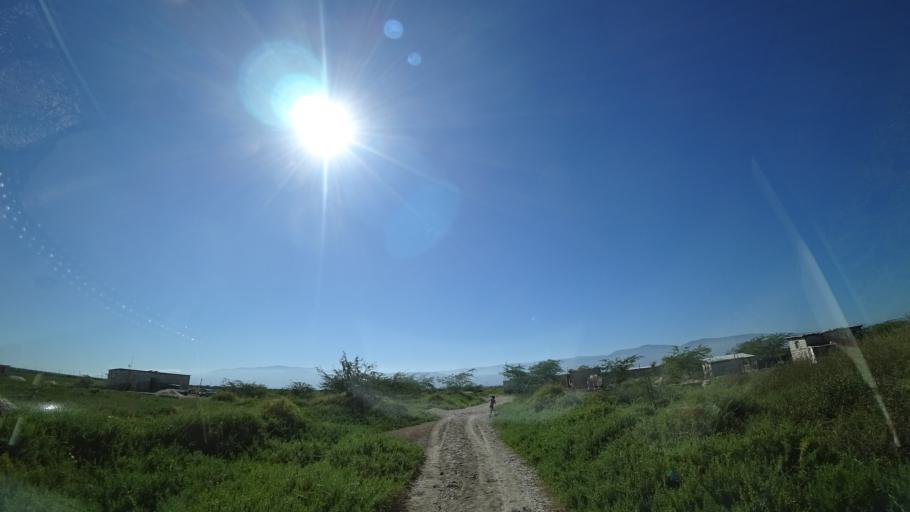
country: HT
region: Ouest
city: Croix des Bouquets
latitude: 18.6581
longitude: -72.2226
